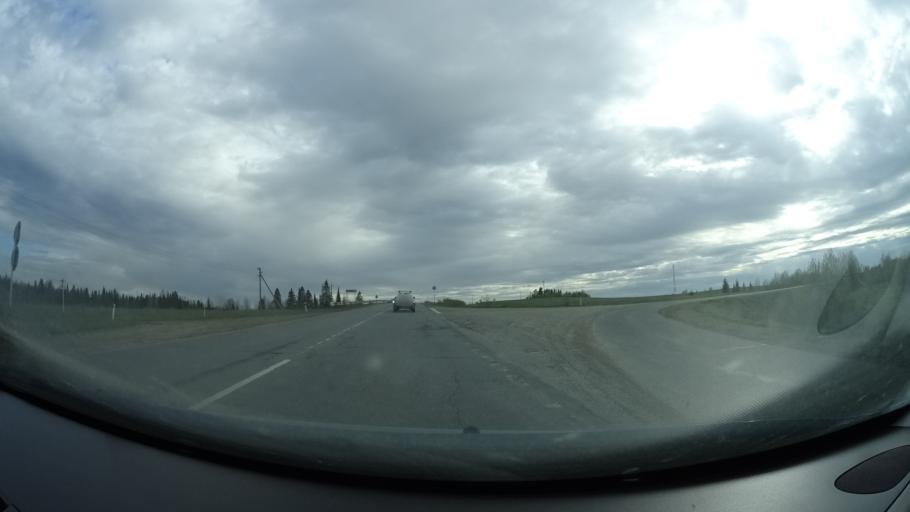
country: RU
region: Perm
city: Yugo-Kamskiy
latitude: 57.7854
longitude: 55.7707
